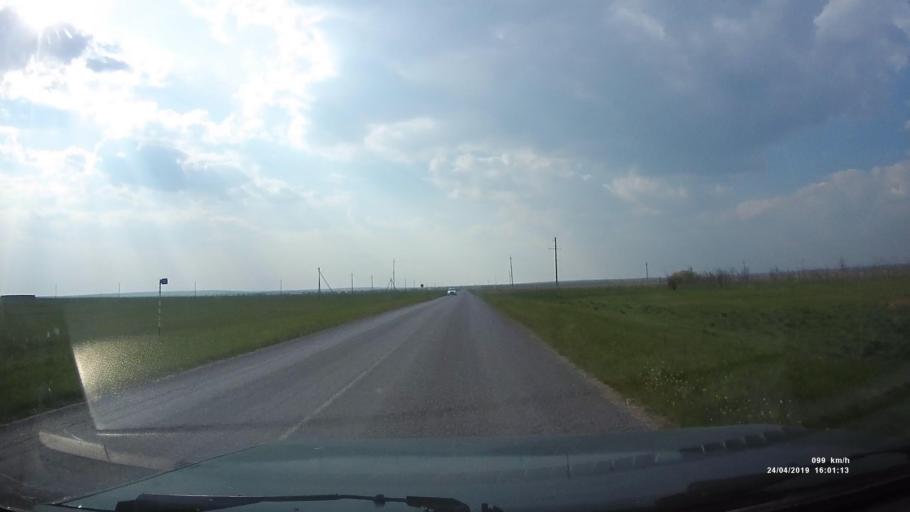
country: RU
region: Rostov
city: Sovetskoye
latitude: 46.6399
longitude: 42.4397
